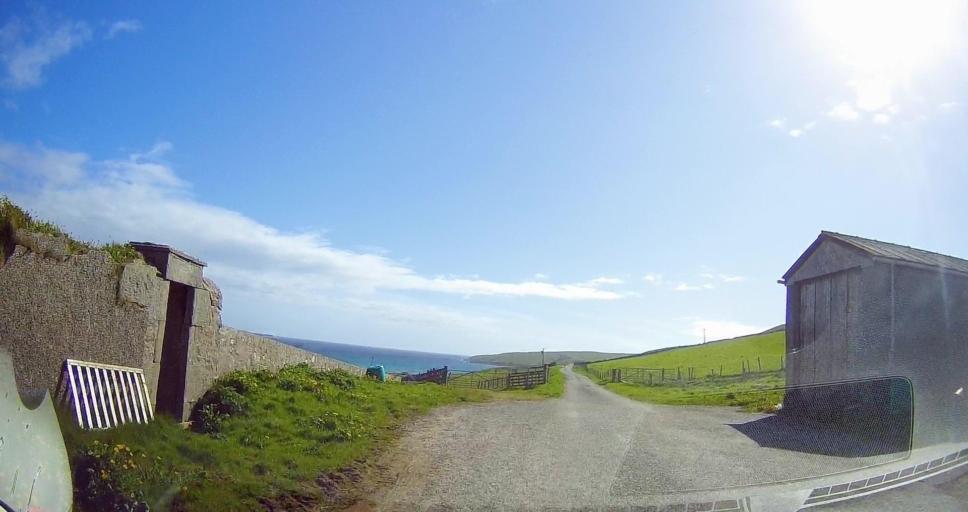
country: GB
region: Scotland
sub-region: Shetland Islands
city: Sandwick
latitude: 59.9016
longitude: -1.3388
